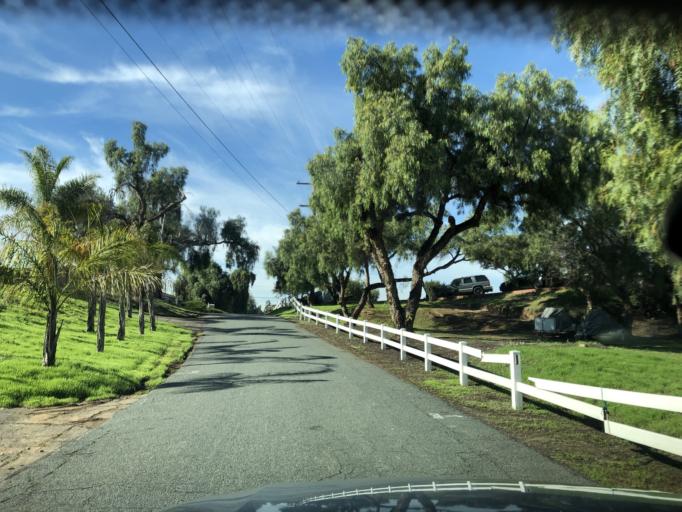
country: US
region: California
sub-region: San Diego County
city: Chula Vista
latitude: 32.6454
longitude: -117.0605
